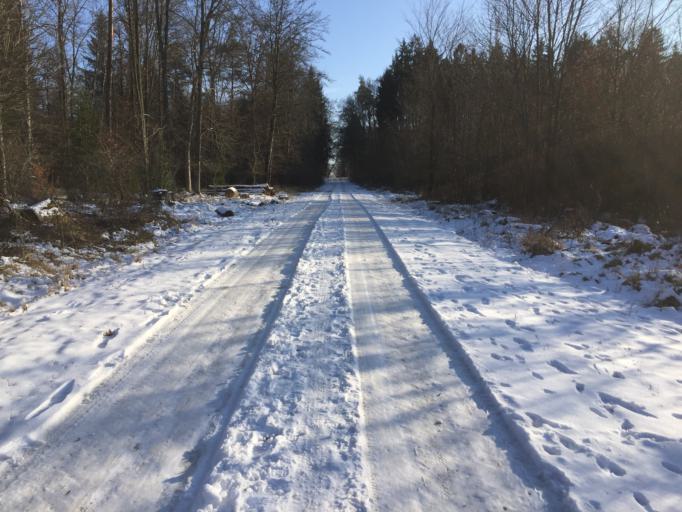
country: DE
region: Baden-Wuerttemberg
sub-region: Regierungsbezirk Stuttgart
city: Weil im Schonbuch
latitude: 48.5731
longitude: 9.0600
